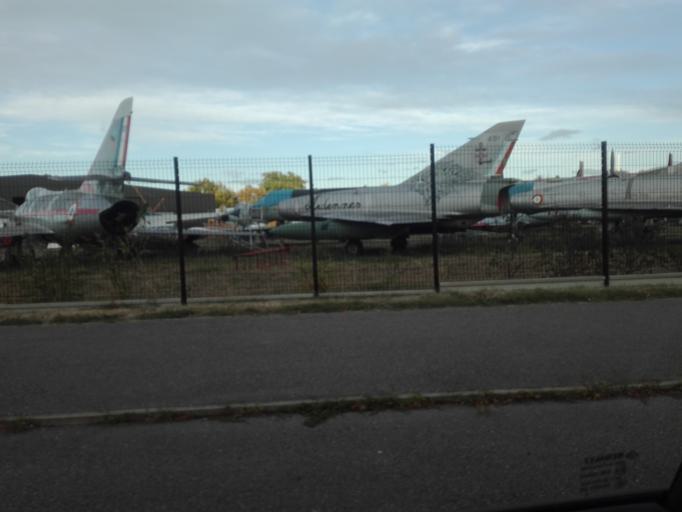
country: FR
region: Midi-Pyrenees
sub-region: Departement de la Haute-Garonne
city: Beauzelle
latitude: 43.6567
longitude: 1.3589
